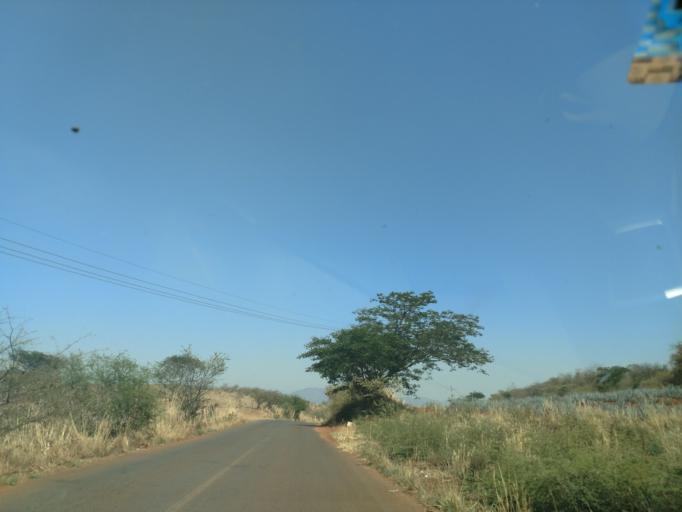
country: MX
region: Nayarit
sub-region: Tepic
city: La Corregidora
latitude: 21.4890
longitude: -104.6796
